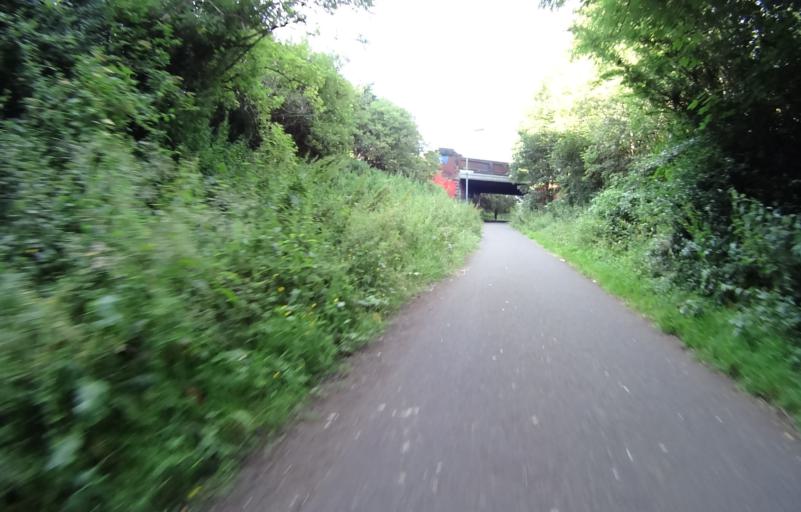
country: GB
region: Scotland
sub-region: Edinburgh
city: Edinburgh
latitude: 55.9607
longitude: -3.2444
